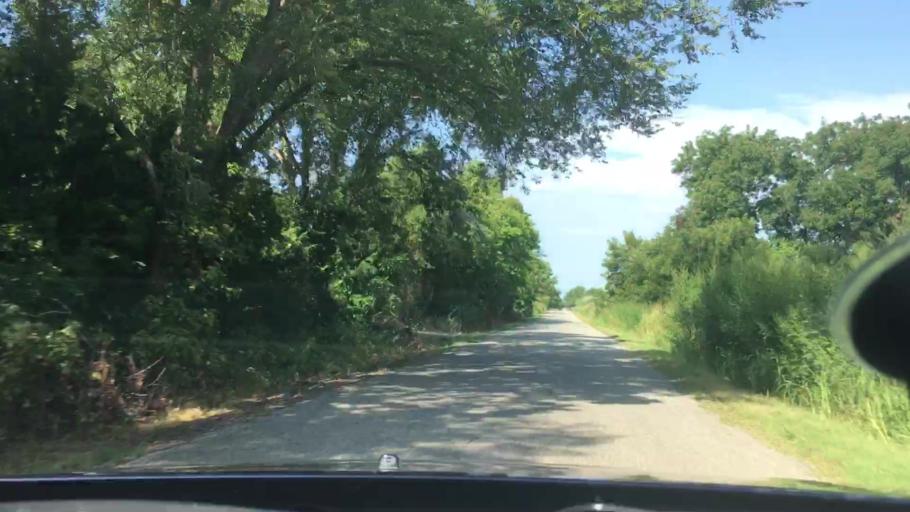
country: US
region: Oklahoma
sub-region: Bryan County
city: Calera
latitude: 33.9110
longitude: -96.4709
